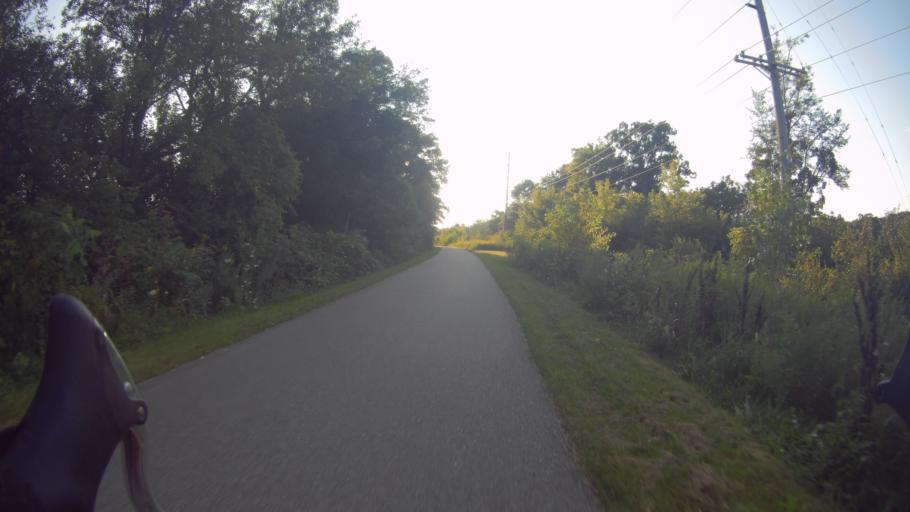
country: US
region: Wisconsin
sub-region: Dane County
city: Shorewood Hills
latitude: 43.0260
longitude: -89.4389
